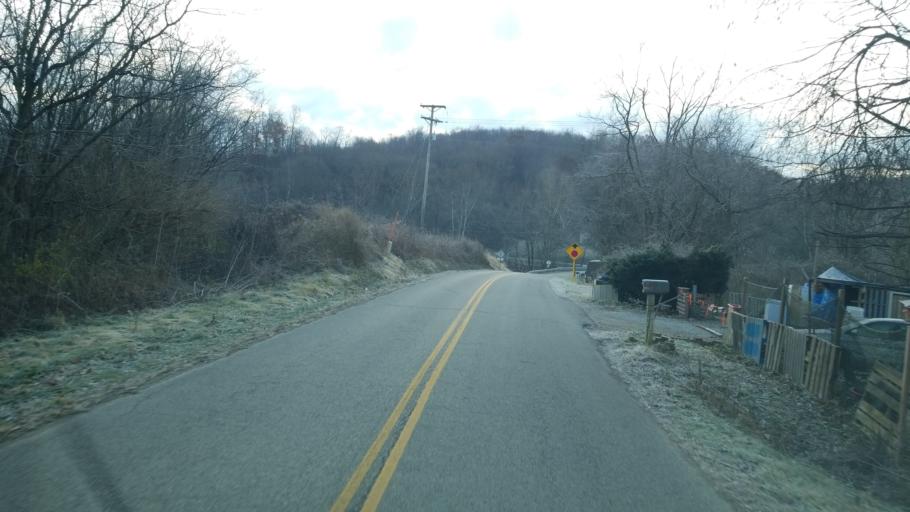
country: US
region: Ohio
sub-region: Ross County
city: Chillicothe
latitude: 39.2352
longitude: -82.8967
